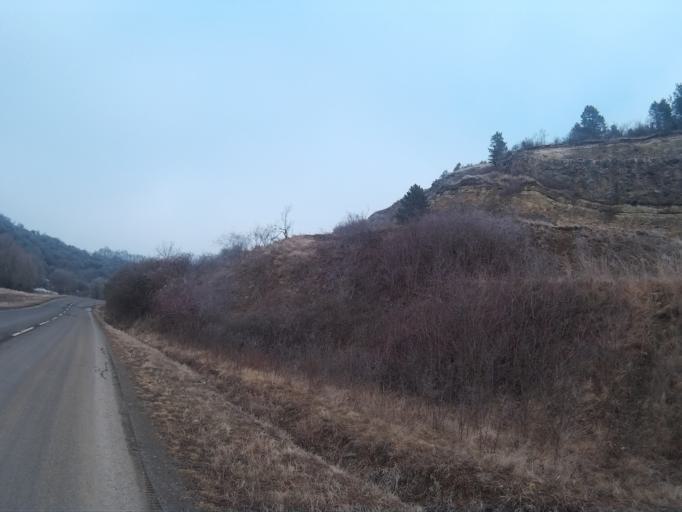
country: HU
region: Nograd
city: Tar
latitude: 47.9913
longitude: 19.7169
